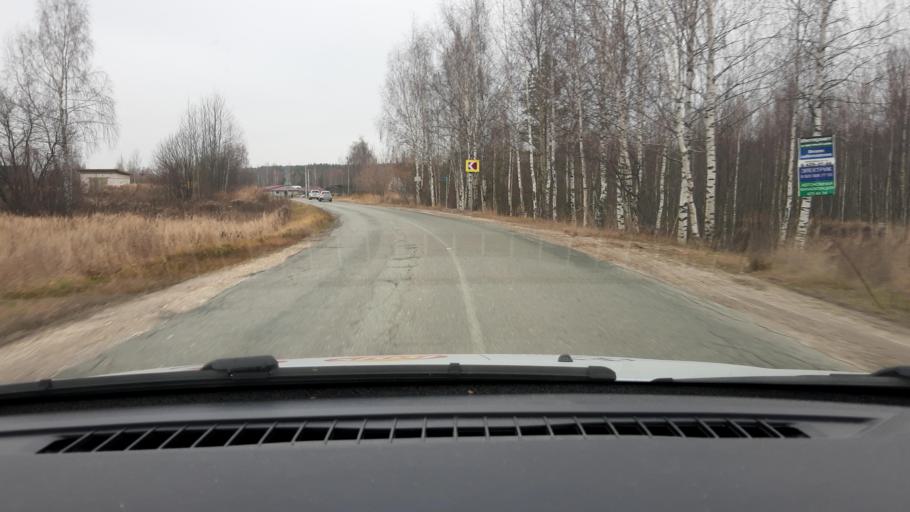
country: RU
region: Nizjnij Novgorod
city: Neklyudovo
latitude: 56.4363
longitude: 43.9211
